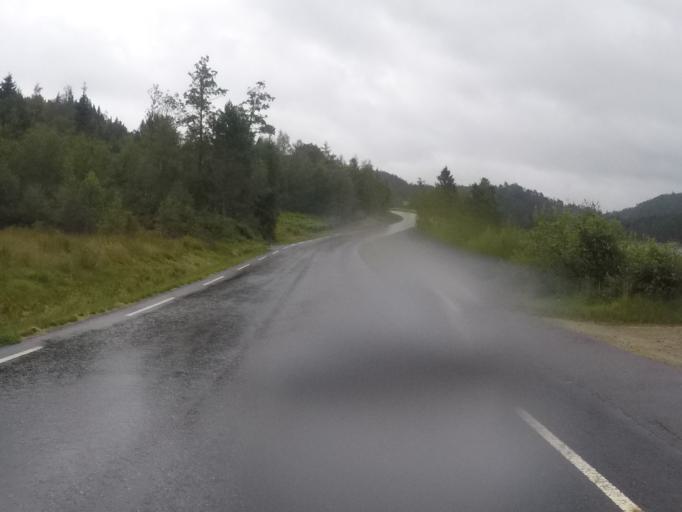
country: NO
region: Vest-Agder
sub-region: Audnedal
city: Konsmo
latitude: 58.2778
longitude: 7.2829
